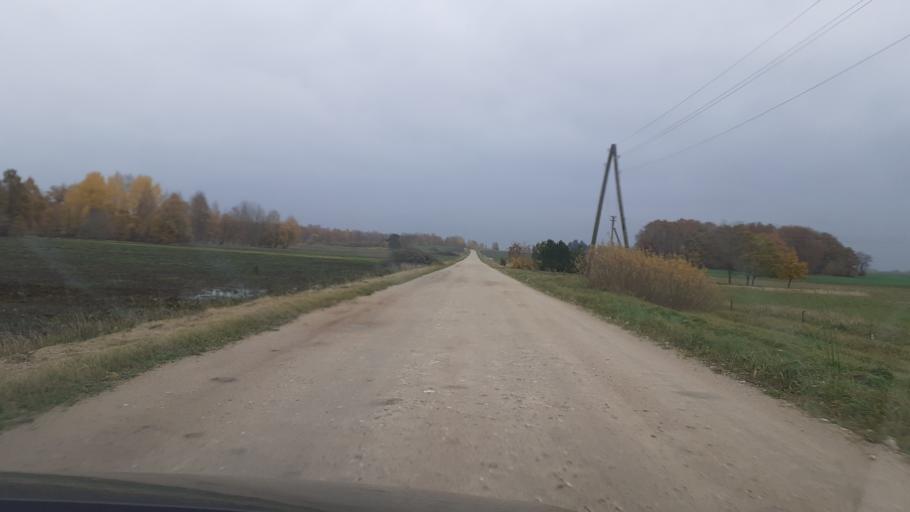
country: LV
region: Saldus Rajons
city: Saldus
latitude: 56.8635
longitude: 22.2805
